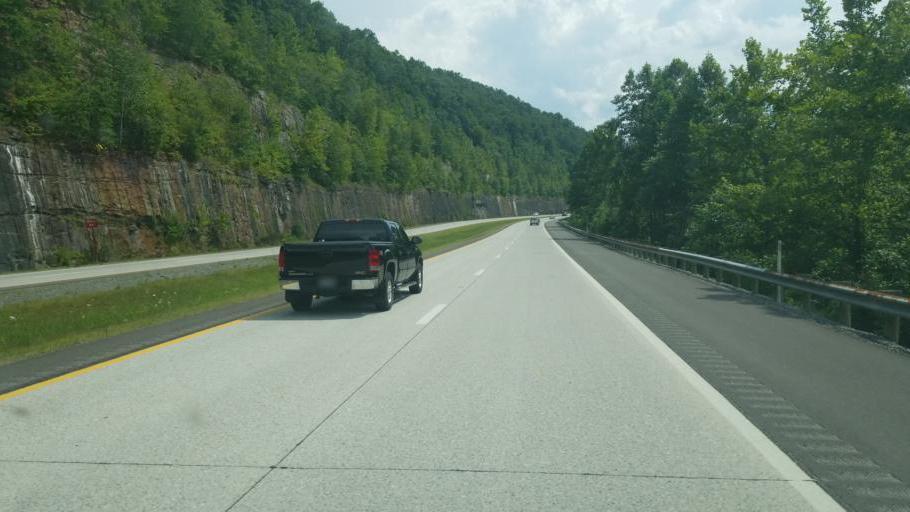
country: US
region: West Virginia
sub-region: Kanawha County
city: Alum Creek
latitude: 38.1949
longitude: -81.8453
